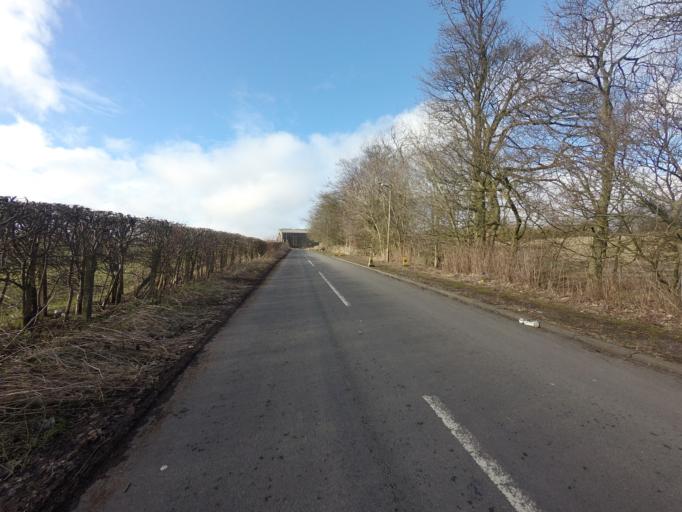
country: GB
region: Scotland
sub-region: West Lothian
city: Livingston
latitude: 55.9177
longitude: -3.5609
